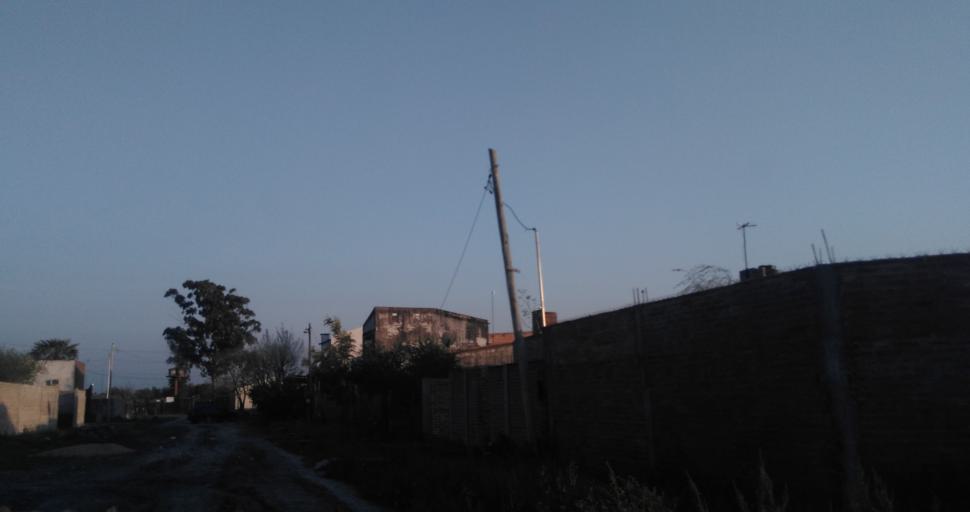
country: AR
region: Chaco
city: Resistencia
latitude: -27.4771
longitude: -59.0138
